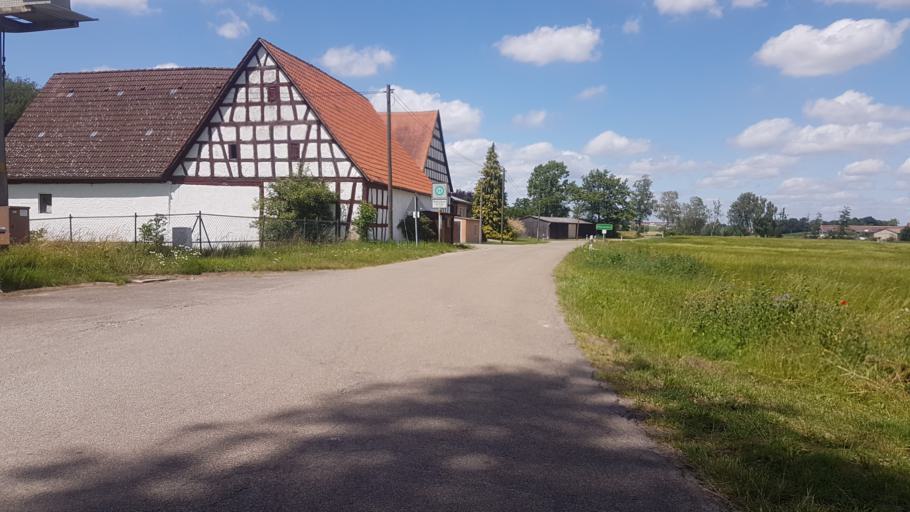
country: DE
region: Bavaria
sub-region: Regierungsbezirk Mittelfranken
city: Leutershausen
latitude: 49.3241
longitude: 10.3771
